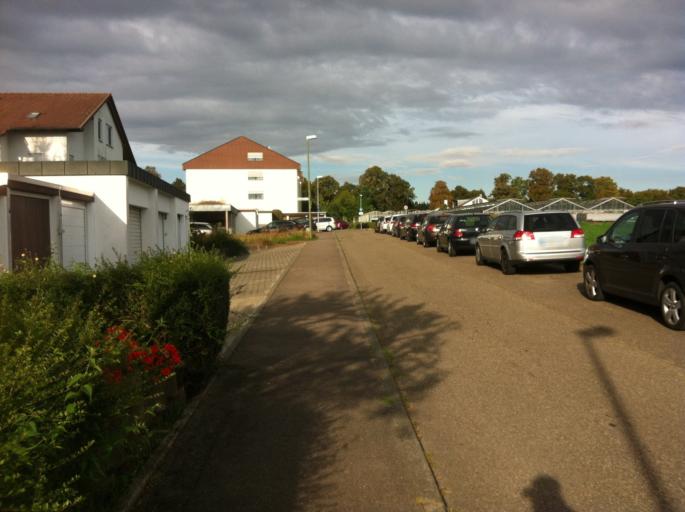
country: DE
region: Baden-Wuerttemberg
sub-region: Regierungsbezirk Stuttgart
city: Kornwestheim
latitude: 48.8714
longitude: 9.1891
